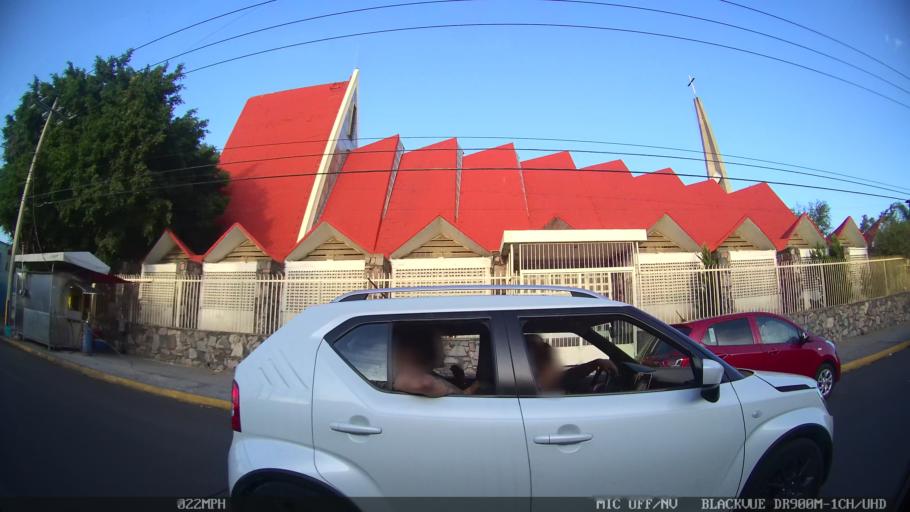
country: MX
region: Jalisco
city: Tlaquepaque
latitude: 20.6867
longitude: -103.3088
